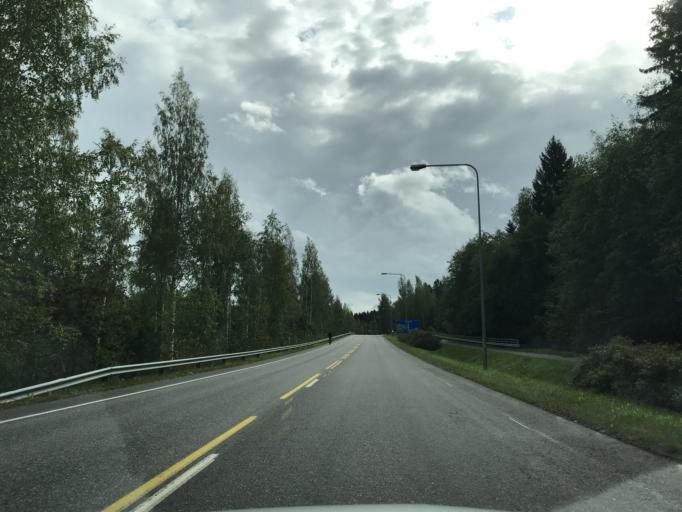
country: FI
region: Paijanne Tavastia
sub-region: Lahti
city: Lahti
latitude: 61.0007
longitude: 25.7790
